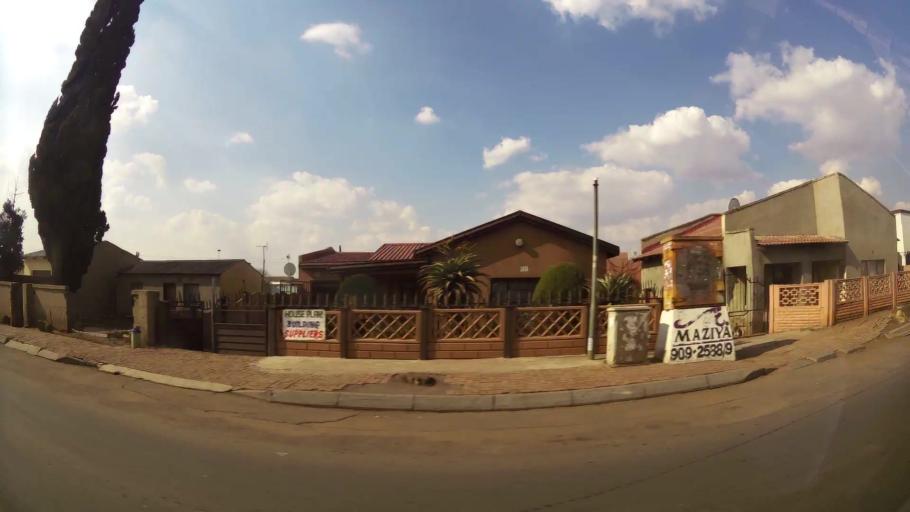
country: ZA
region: Gauteng
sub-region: Ekurhuleni Metropolitan Municipality
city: Germiston
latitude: -26.3133
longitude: 28.1570
